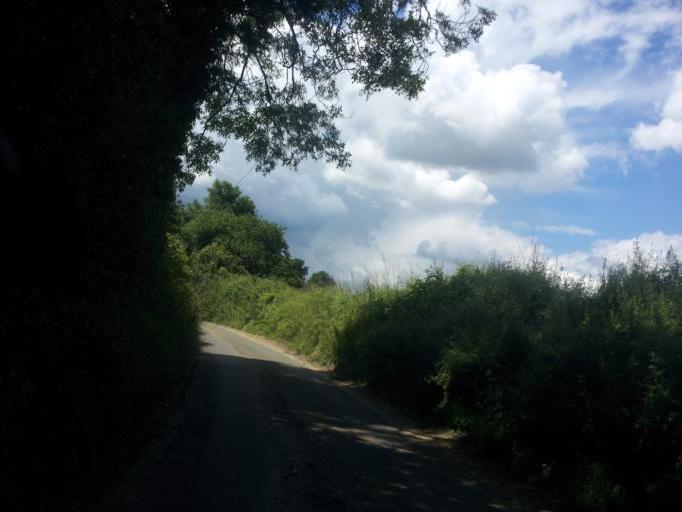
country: GB
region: England
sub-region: Kent
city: West Malling
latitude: 51.3112
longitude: 0.3730
